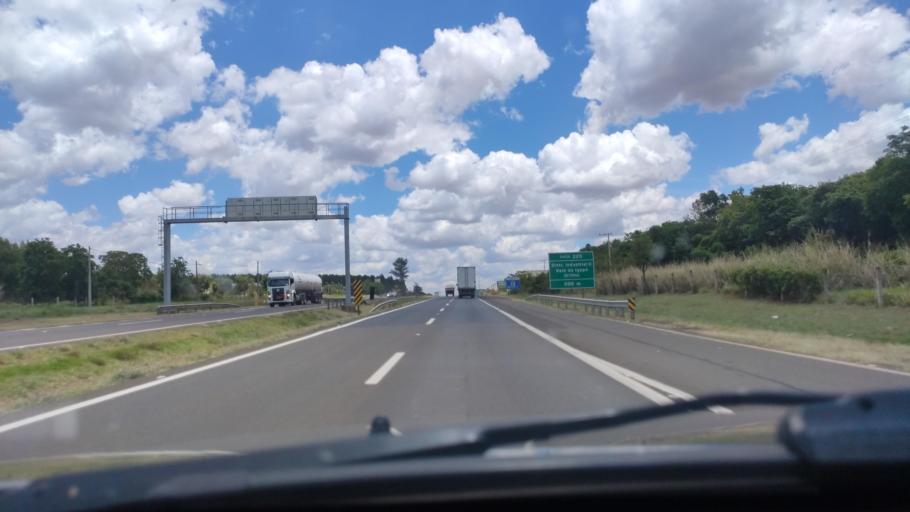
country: BR
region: Sao Paulo
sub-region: Bauru
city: Bauru
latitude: -22.3218
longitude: -48.9675
